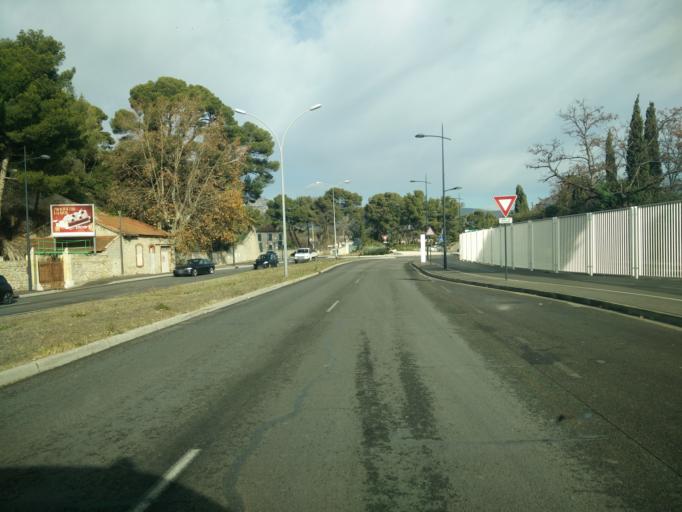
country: FR
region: Provence-Alpes-Cote d'Azur
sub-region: Departement du Var
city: La Seyne-sur-Mer
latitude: 43.1121
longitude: 5.8832
